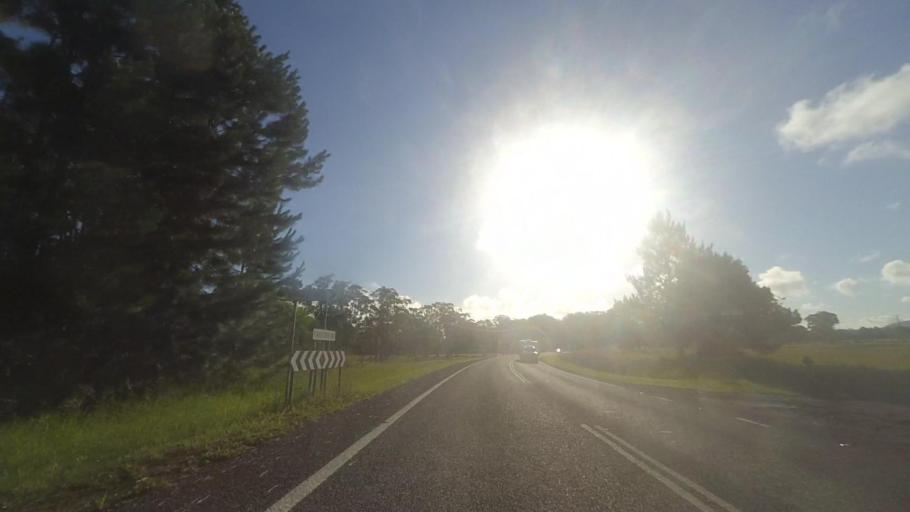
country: AU
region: New South Wales
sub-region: Great Lakes
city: Nabiac
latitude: -32.0918
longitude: 152.4551
